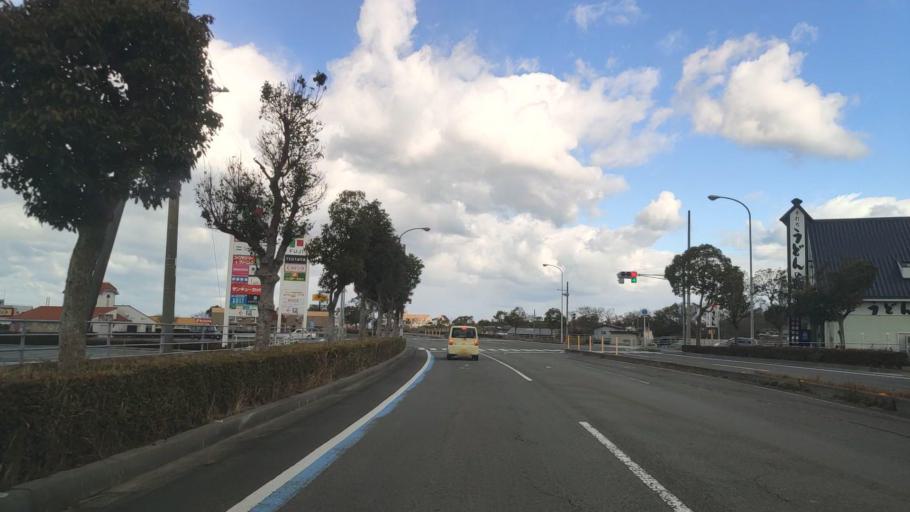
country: JP
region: Ehime
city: Hojo
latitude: 33.9451
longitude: 132.7761
